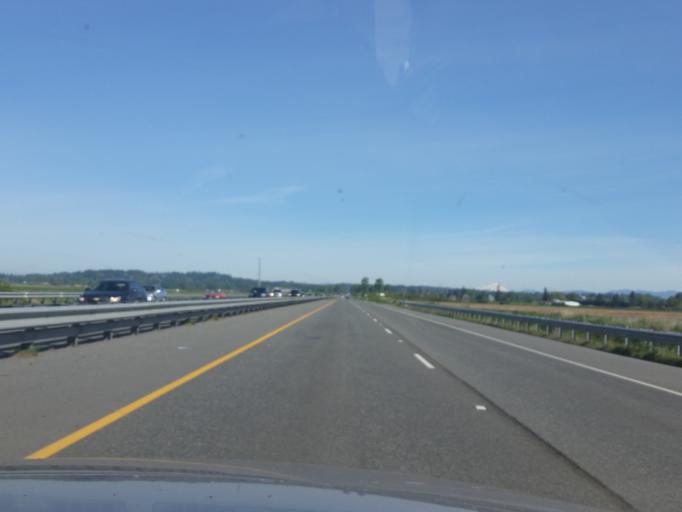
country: US
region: Washington
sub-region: Snohomish County
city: Snohomish
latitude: 47.8837
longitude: -122.1096
